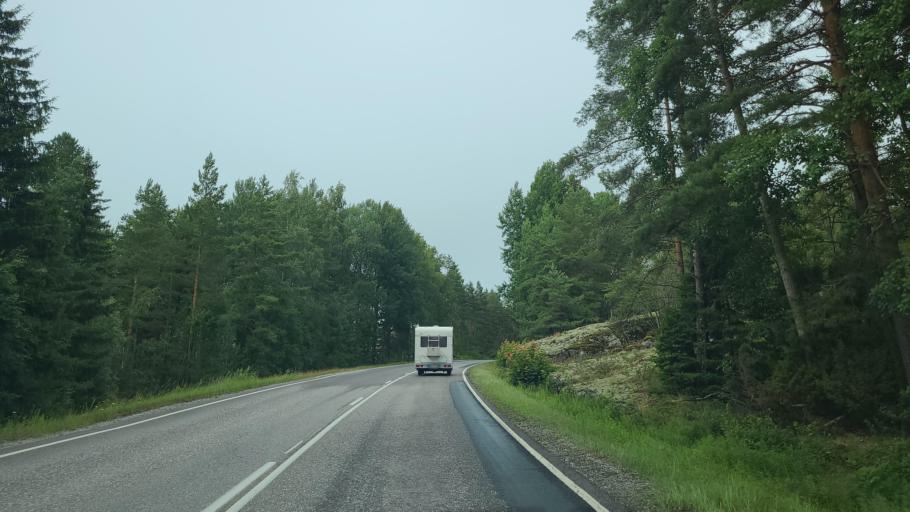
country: FI
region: Varsinais-Suomi
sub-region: Turku
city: Sauvo
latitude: 60.3011
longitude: 22.6807
